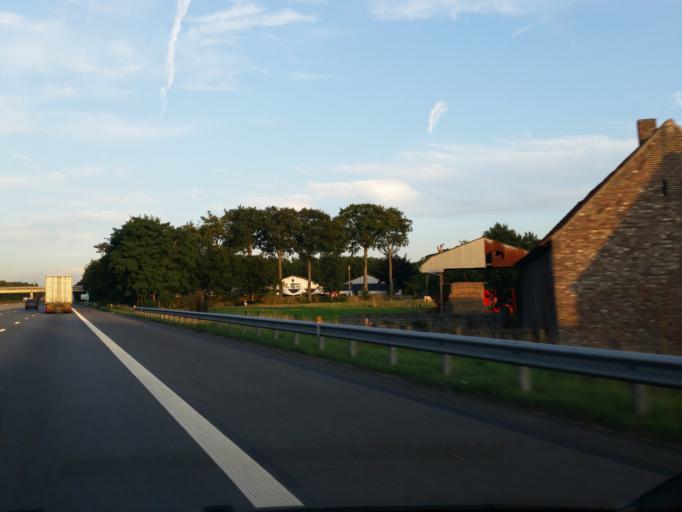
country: BE
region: Flanders
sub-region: Provincie West-Vlaanderen
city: Zedelgem
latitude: 51.1677
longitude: 3.1682
